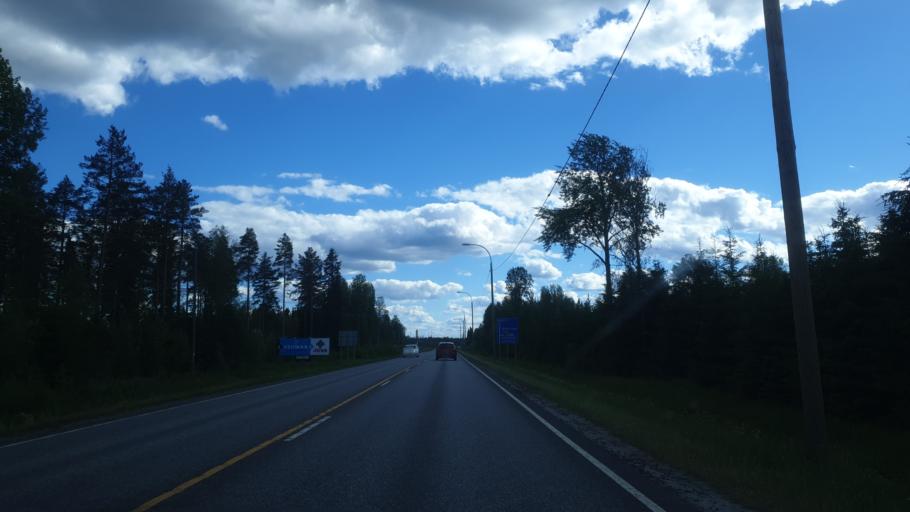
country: FI
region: Southern Savonia
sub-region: Pieksaemaeki
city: Juva
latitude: 61.9072
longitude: 27.8050
